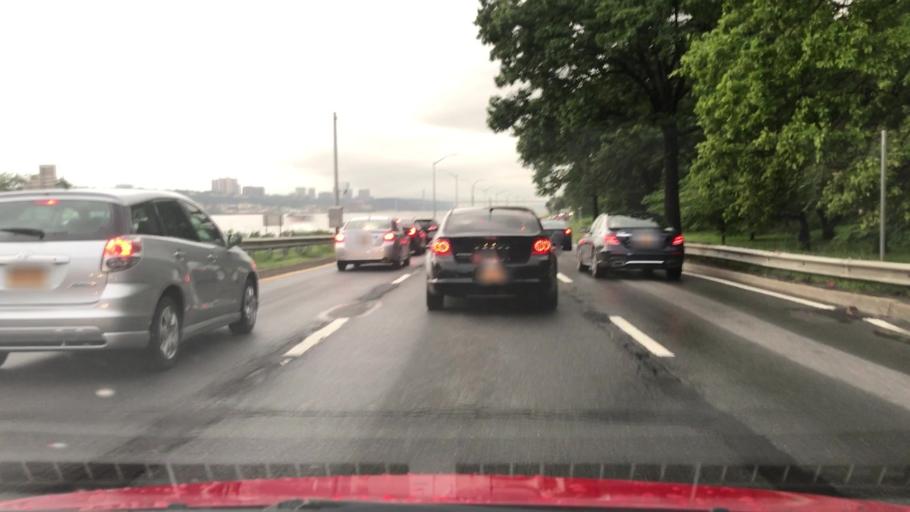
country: US
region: New York
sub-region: New York County
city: Manhattan
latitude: 40.7889
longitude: -73.9821
